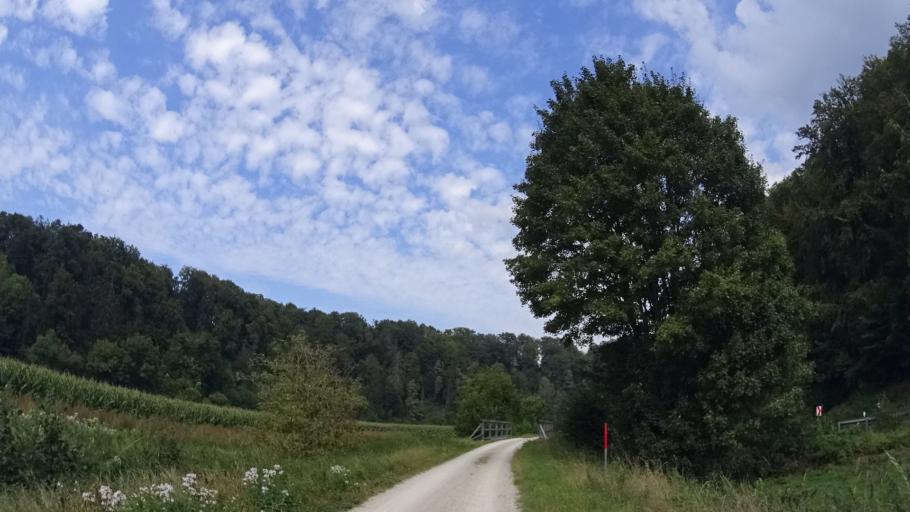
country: DE
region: Bavaria
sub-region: Lower Bavaria
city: Riedenburg
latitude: 48.9122
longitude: 11.6776
